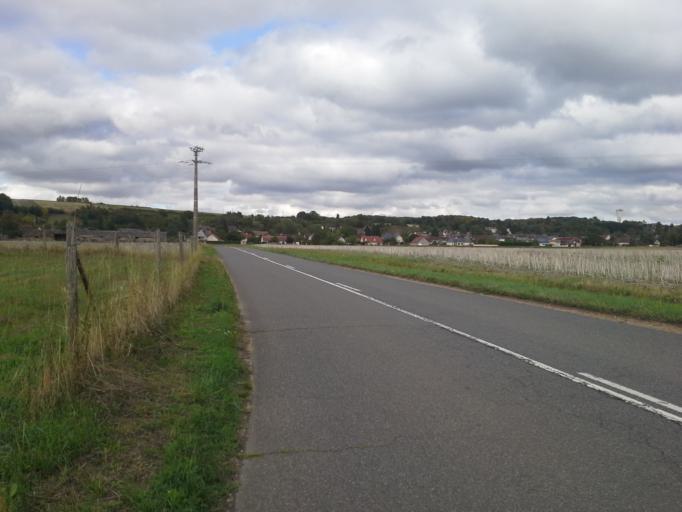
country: FR
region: Centre
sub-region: Departement du Loir-et-Cher
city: Villiers-sur-Loir
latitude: 47.8046
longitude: 0.9831
